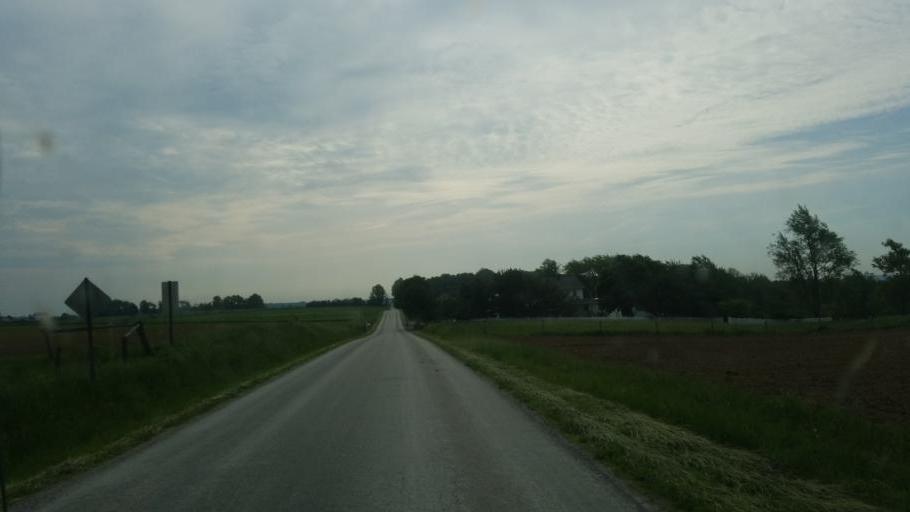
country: US
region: Ohio
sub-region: Wayne County
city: Apple Creek
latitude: 40.6824
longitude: -81.7643
